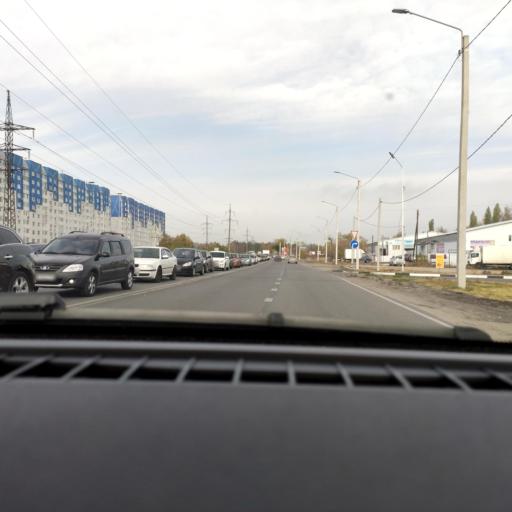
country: RU
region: Voronezj
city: Maslovka
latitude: 51.5913
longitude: 39.2485
